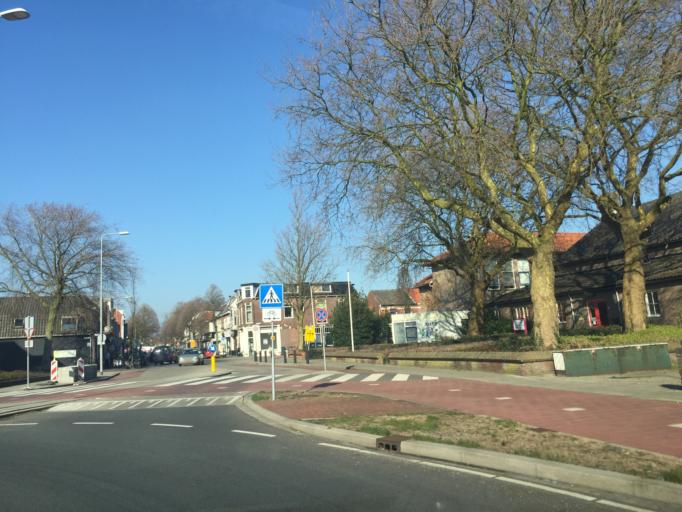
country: NL
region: South Holland
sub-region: Gemeente Hillegom
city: Hillegom
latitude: 52.2891
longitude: 4.5773
